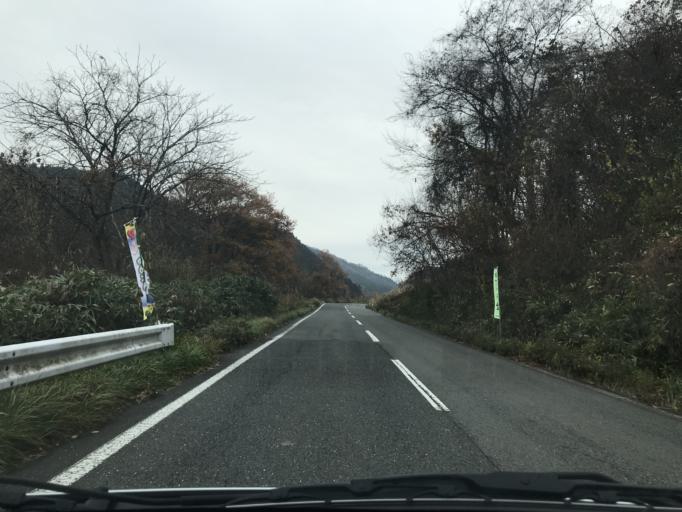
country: JP
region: Iwate
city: Kitakami
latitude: 39.2685
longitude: 141.1804
